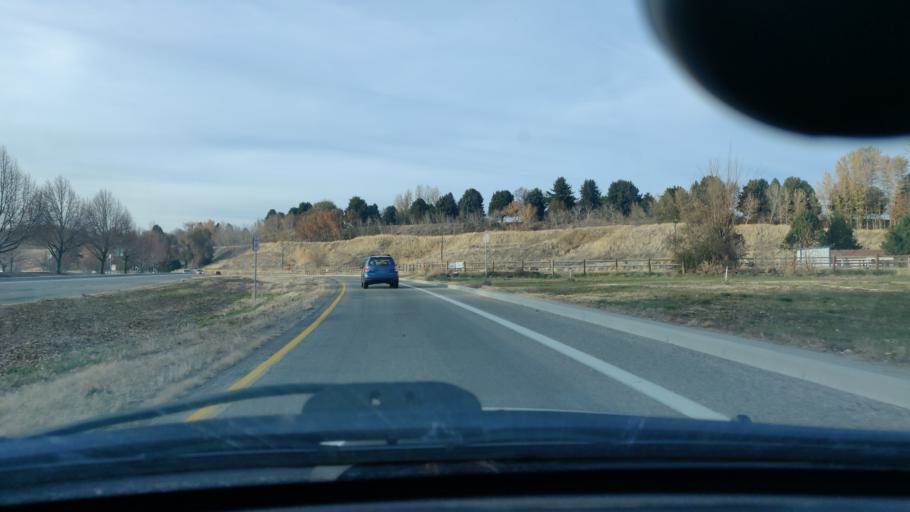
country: US
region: Idaho
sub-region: Ada County
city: Eagle
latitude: 43.6887
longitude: -116.3027
